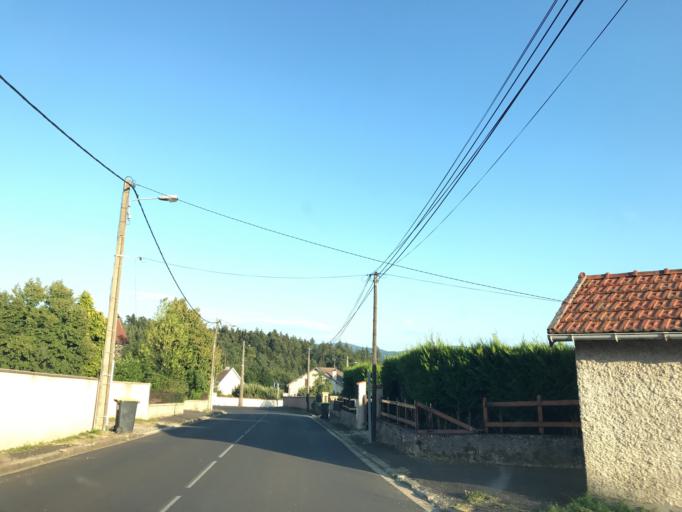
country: FR
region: Auvergne
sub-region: Departement du Puy-de-Dome
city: Saint-Remy-sur-Durolle
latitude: 45.8883
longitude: 3.5971
